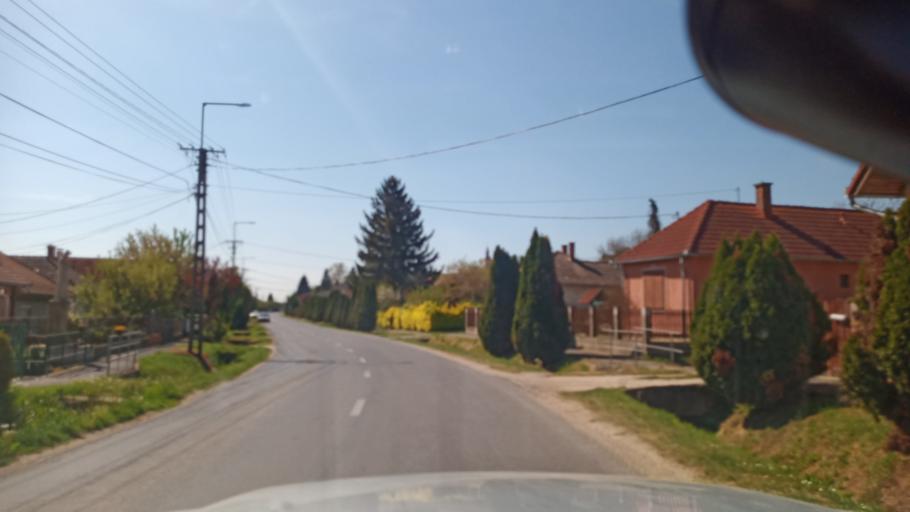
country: HU
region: Zala
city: Sarmellek
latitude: 46.7420
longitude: 17.1063
